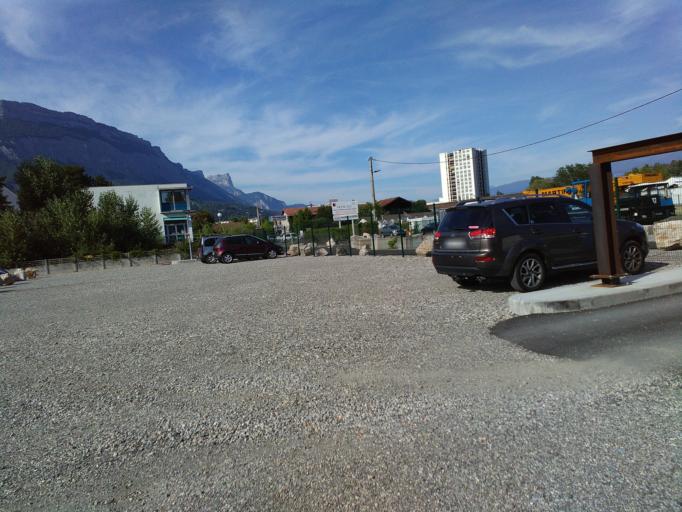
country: FR
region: Rhone-Alpes
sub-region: Departement de l'Isere
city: La Tronche
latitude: 45.1953
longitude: 5.7470
